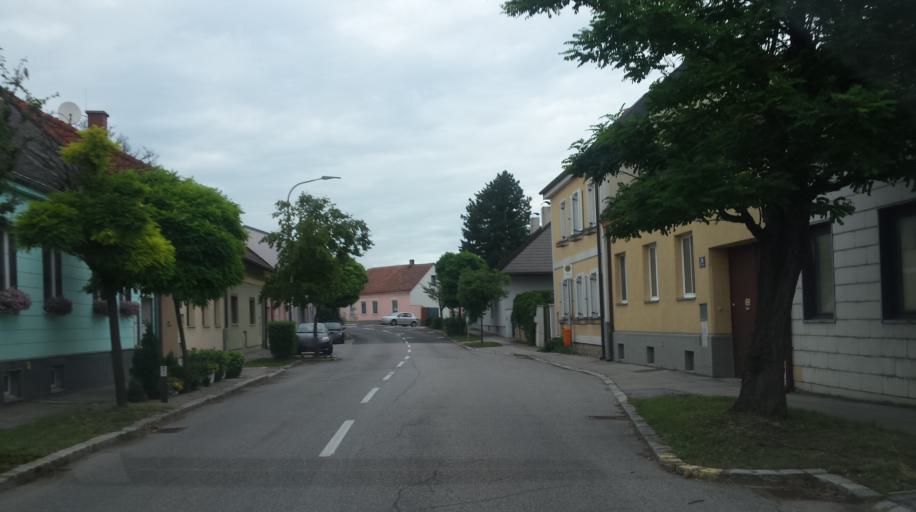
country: AT
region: Lower Austria
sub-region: Politischer Bezirk Wien-Umgebung
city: Zwolfaxing
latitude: 48.1124
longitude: 16.4603
